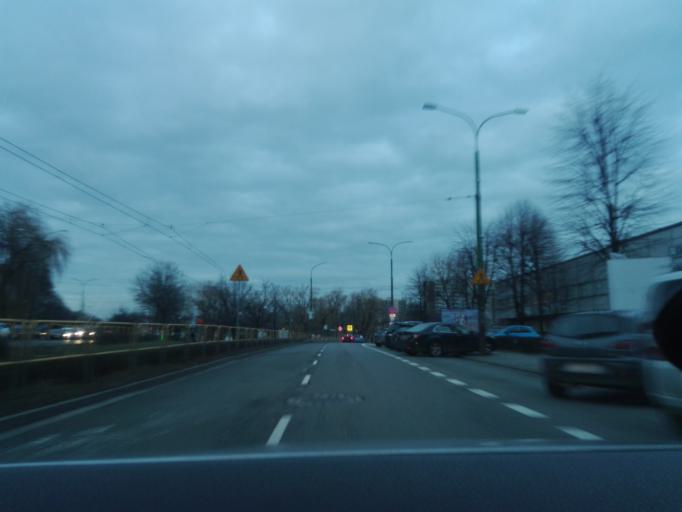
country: PL
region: Silesian Voivodeship
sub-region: Katowice
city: Katowice
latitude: 50.2722
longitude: 19.0249
